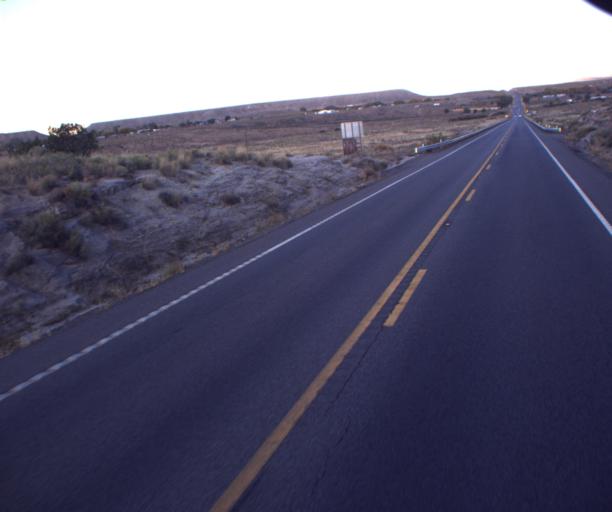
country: US
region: New Mexico
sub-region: San Juan County
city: Shiprock
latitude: 36.9254
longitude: -109.0955
